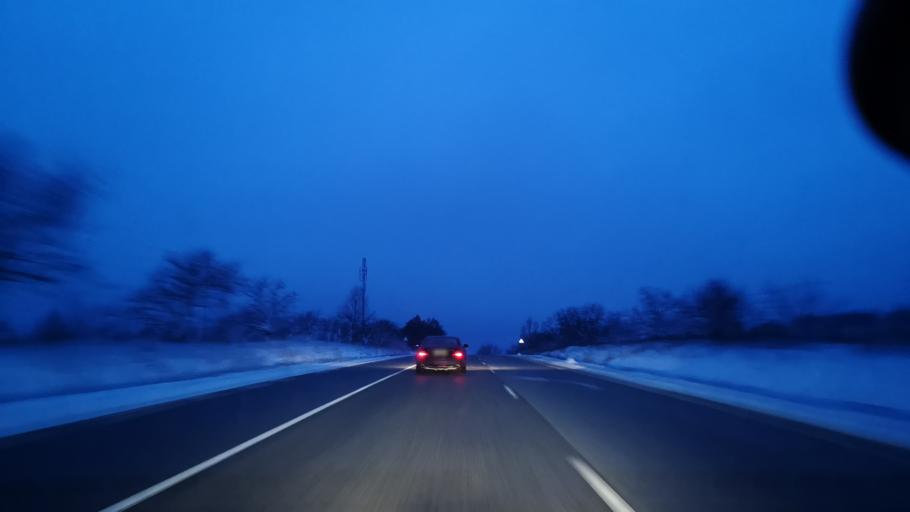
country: MD
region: Orhei
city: Orhei
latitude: 47.5371
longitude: 28.7934
